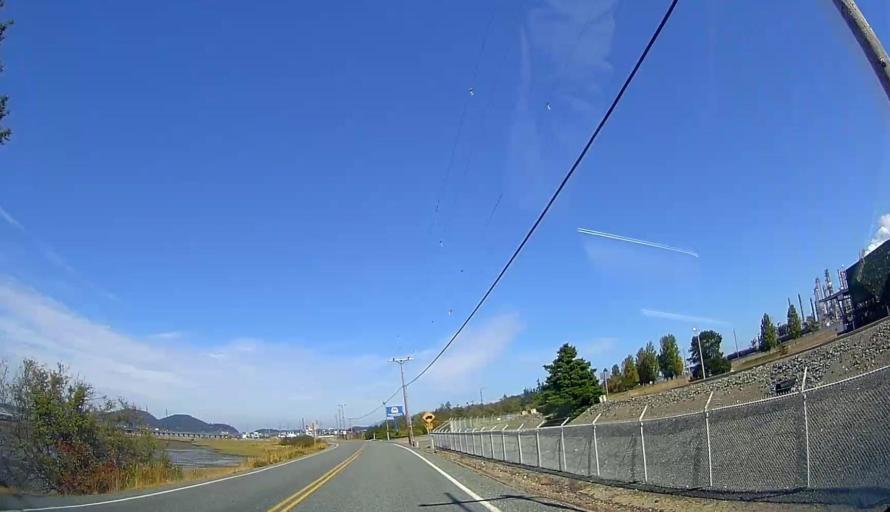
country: US
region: Washington
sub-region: Skagit County
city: Anacortes
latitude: 48.4922
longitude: -122.5748
